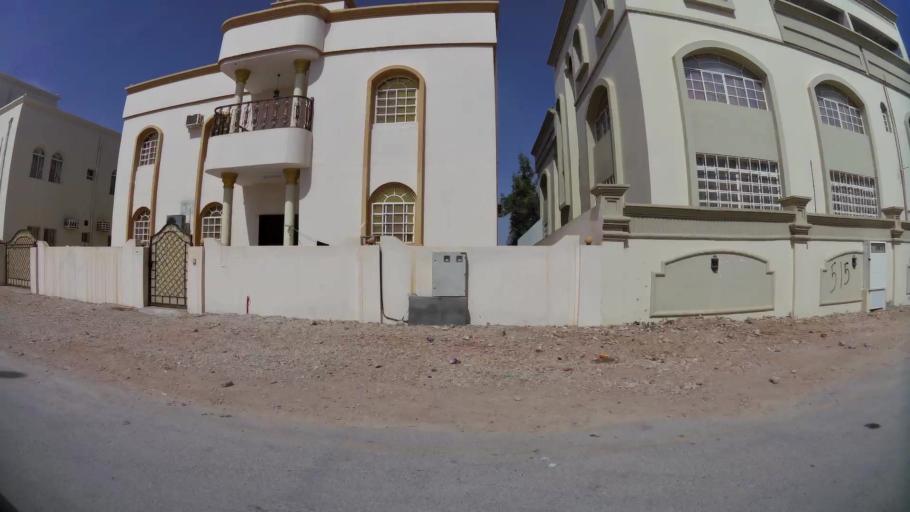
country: OM
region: Zufar
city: Salalah
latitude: 17.0455
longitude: 54.1539
